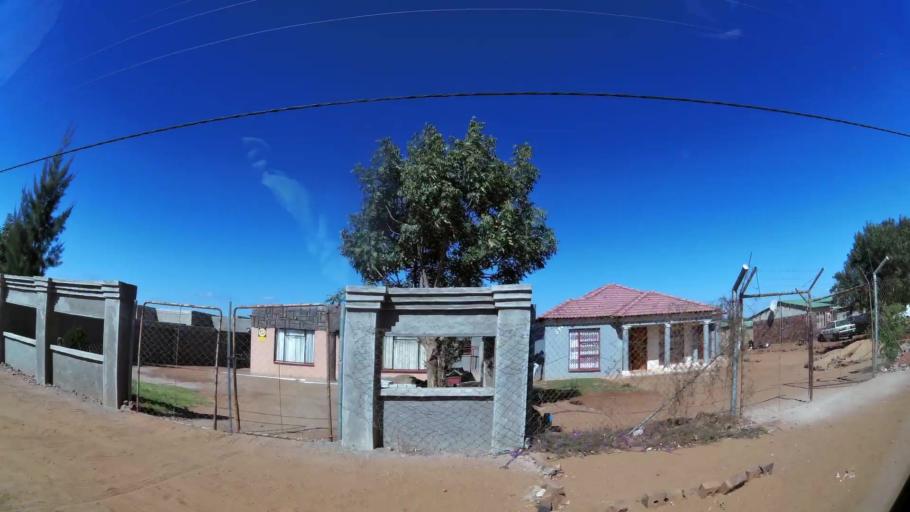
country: ZA
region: Limpopo
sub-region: Capricorn District Municipality
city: Polokwane
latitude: -23.8971
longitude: 29.4153
